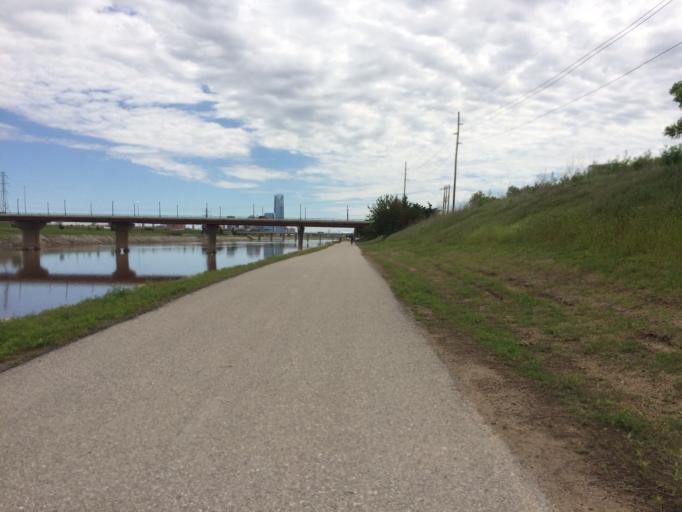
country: US
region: Oklahoma
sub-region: Oklahoma County
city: Oklahoma City
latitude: 35.4583
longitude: -97.5571
